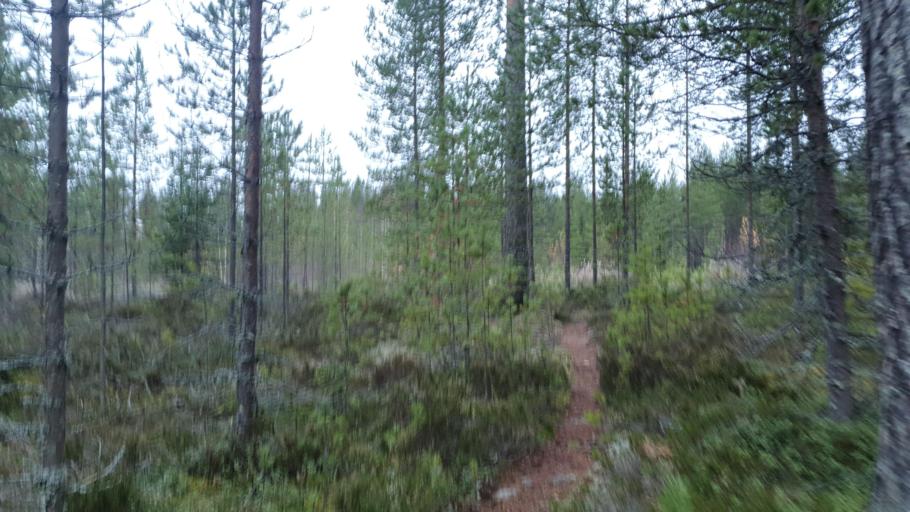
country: FI
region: Kainuu
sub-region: Kehys-Kainuu
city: Kuhmo
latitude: 64.1301
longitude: 29.3957
